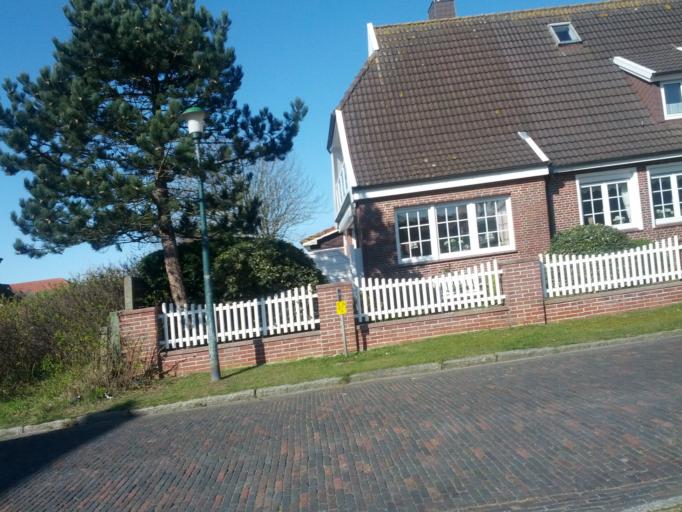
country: DE
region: Lower Saxony
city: Langeoog
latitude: 53.7512
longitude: 7.4889
